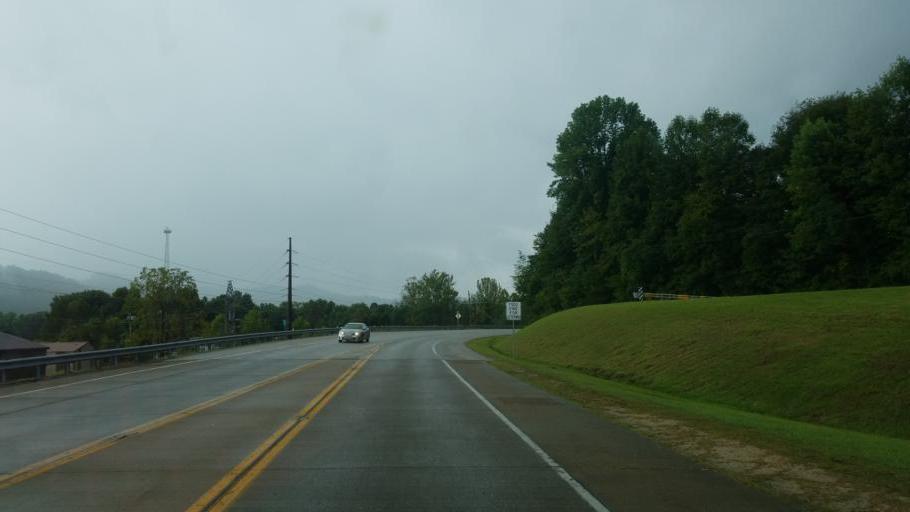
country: US
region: Kentucky
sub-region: Rowan County
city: Morehead
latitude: 38.1689
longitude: -83.4400
